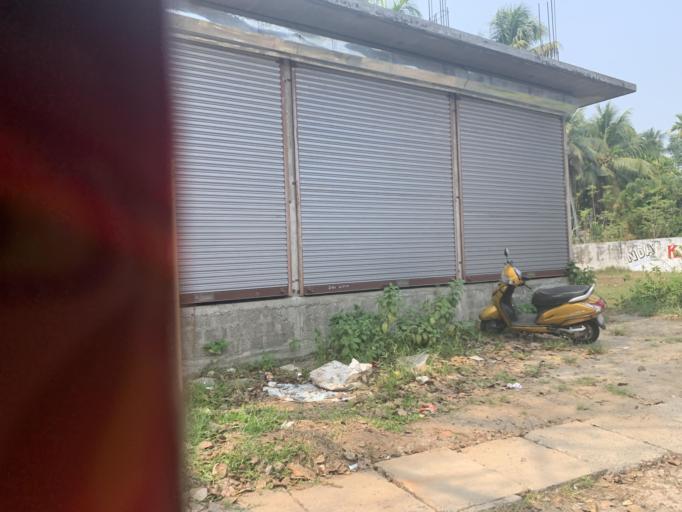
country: IN
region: Kerala
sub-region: Ernakulam
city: Cochin
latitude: 9.9418
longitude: 76.3071
